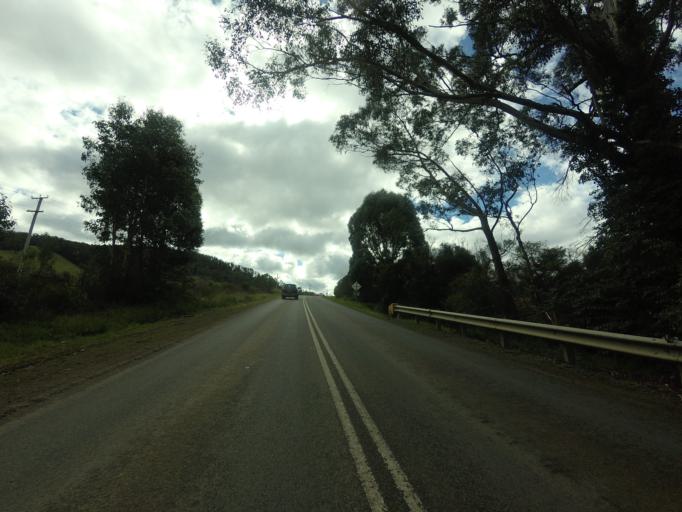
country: AU
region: Tasmania
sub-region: Huon Valley
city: Geeveston
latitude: -43.1890
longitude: 146.9589
